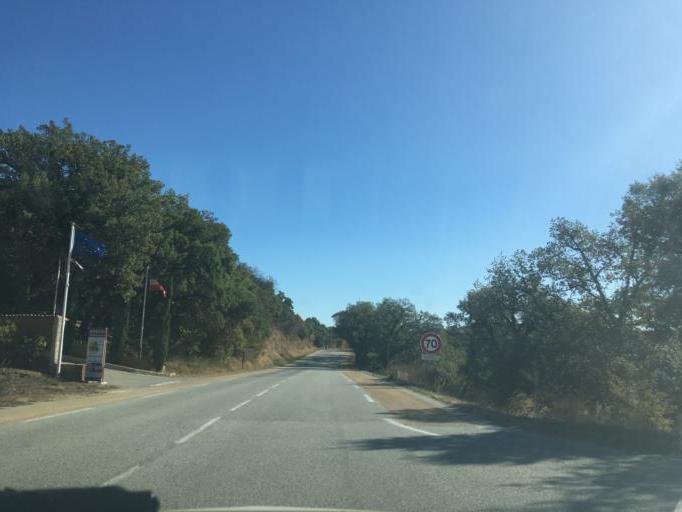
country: FR
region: Provence-Alpes-Cote d'Azur
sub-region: Departement du Var
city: Grimaud
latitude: 43.2882
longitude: 6.4982
